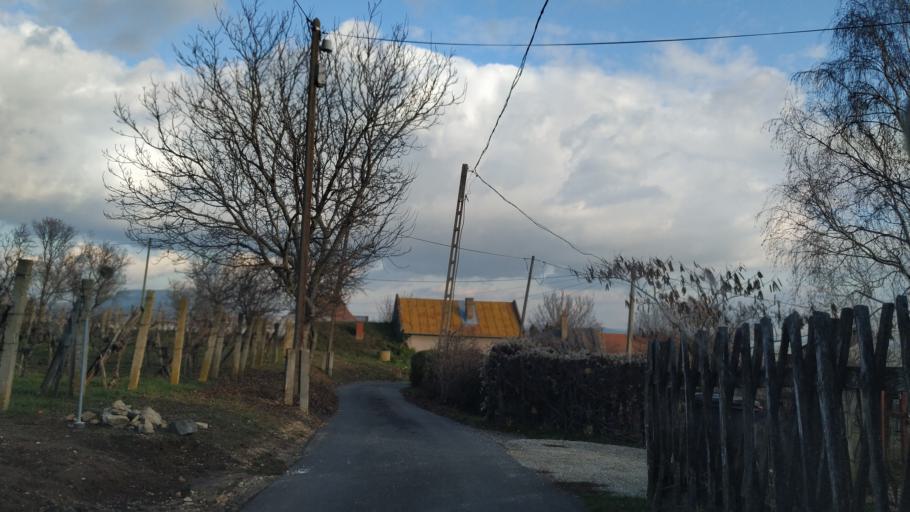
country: HU
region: Zala
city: Vonyarcvashegy
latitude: 46.7865
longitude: 17.3693
